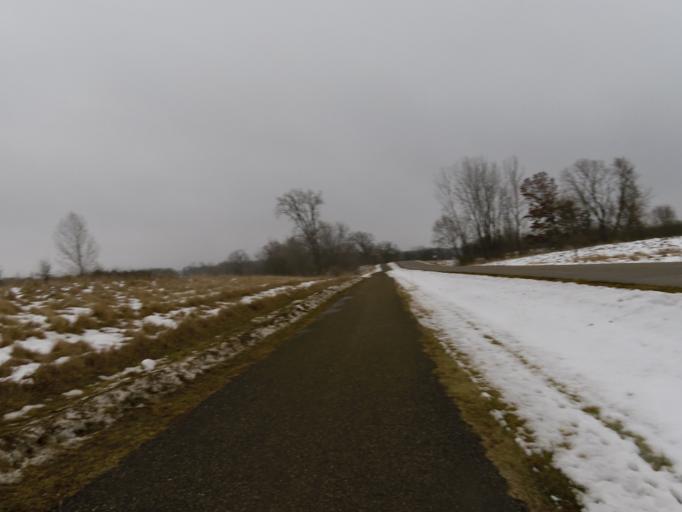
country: US
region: Minnesota
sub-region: Washington County
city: Lake Elmo
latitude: 44.9887
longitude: -92.8892
